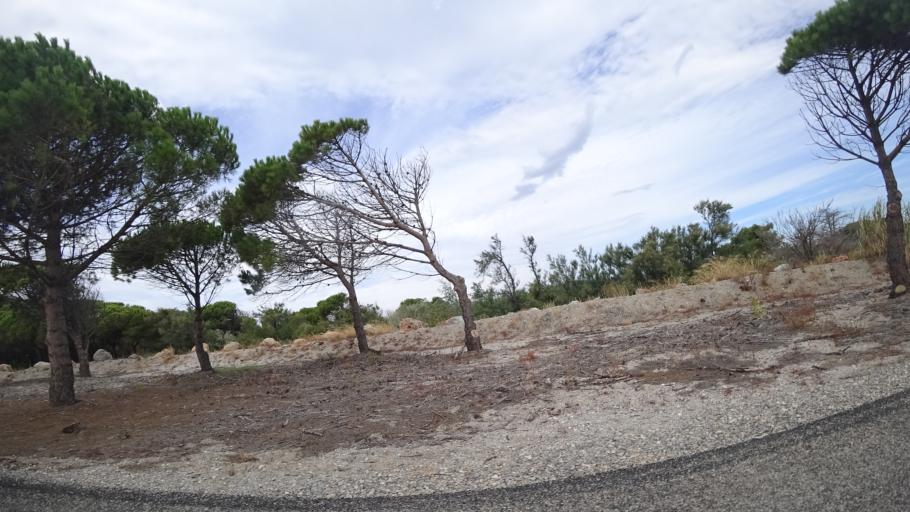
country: FR
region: Languedoc-Roussillon
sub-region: Departement de l'Aude
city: Leucate
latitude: 42.8672
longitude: 3.0325
